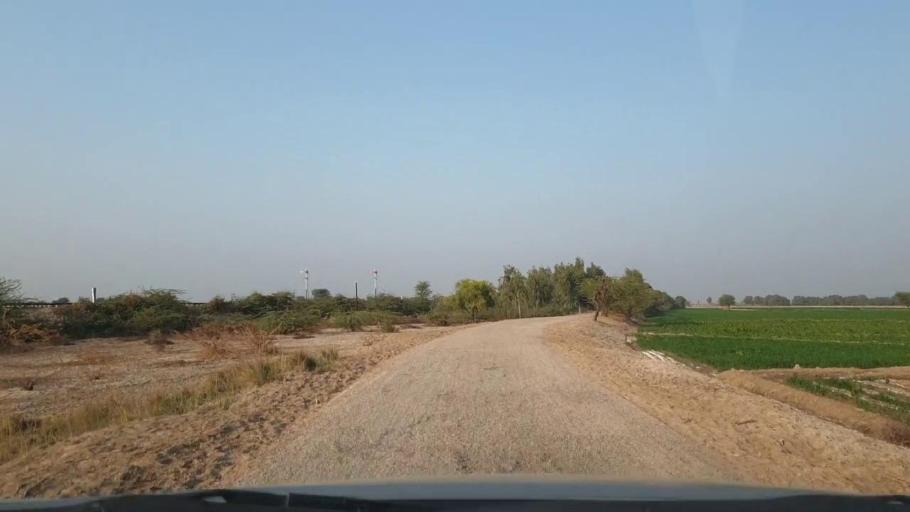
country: PK
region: Sindh
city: Tando Adam
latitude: 25.6917
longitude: 68.6341
